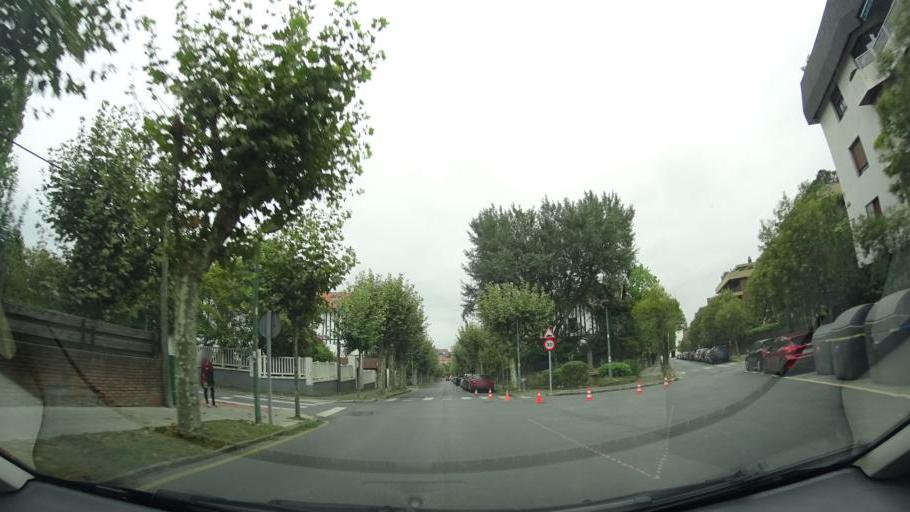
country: ES
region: Basque Country
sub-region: Bizkaia
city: Algorta
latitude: 43.3383
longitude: -3.0064
